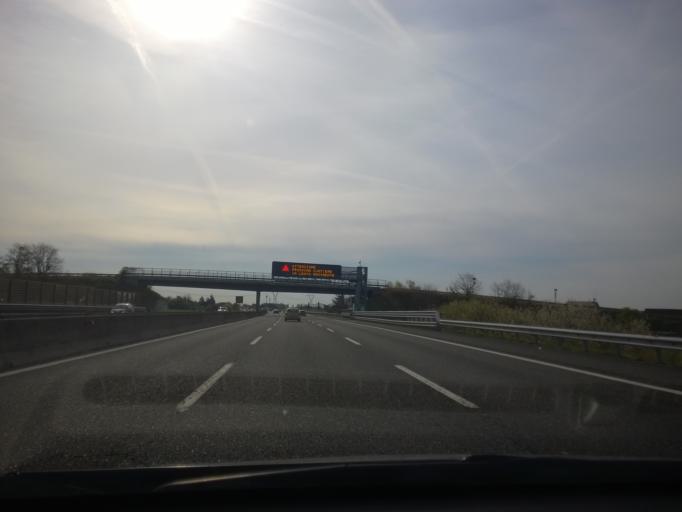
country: IT
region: Emilia-Romagna
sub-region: Forli-Cesena
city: Cesena
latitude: 44.1760
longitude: 12.2696
